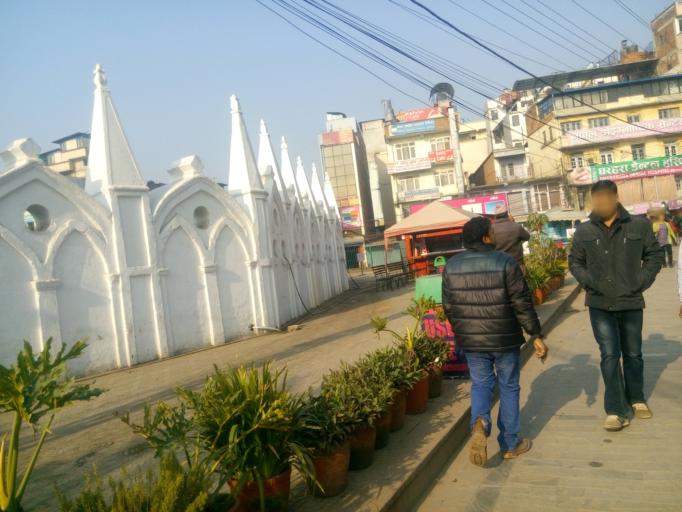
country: NP
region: Central Region
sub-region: Bagmati Zone
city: Kathmandu
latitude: 27.7004
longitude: 85.3122
